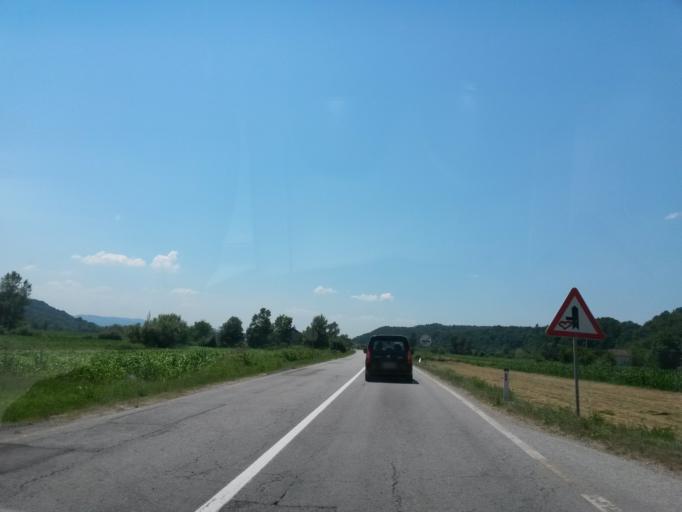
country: BA
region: Federation of Bosnia and Herzegovina
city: Lukavica
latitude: 44.8990
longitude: 18.0970
